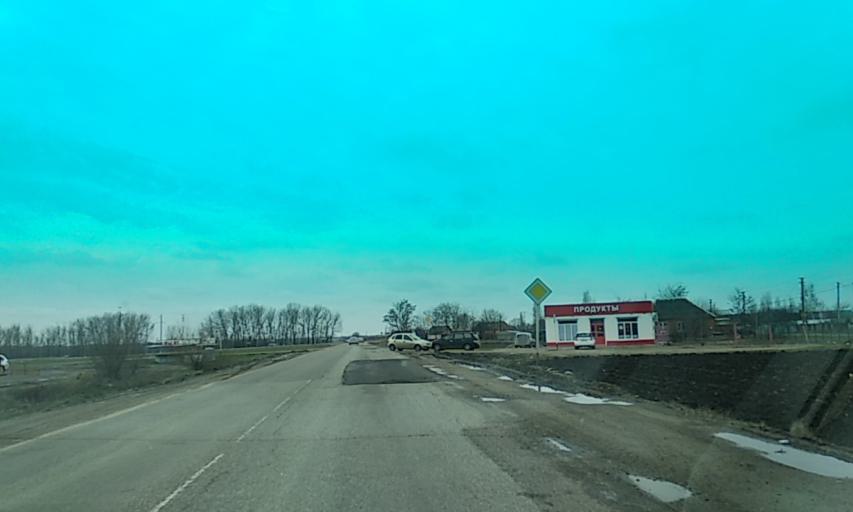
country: RU
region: Krasnodarskiy
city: Ust'-Labinsk
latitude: 45.3682
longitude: 39.7007
